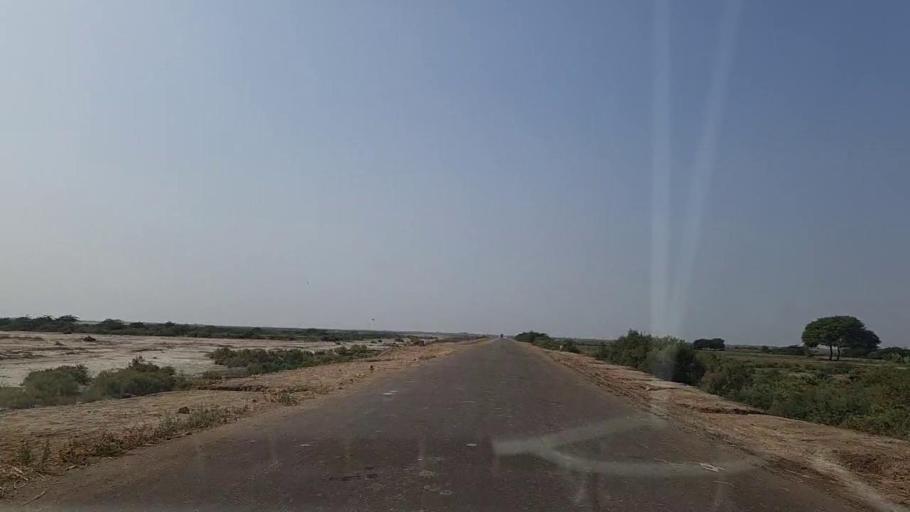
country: PK
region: Sindh
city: Chuhar Jamali
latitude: 24.2218
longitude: 67.8971
